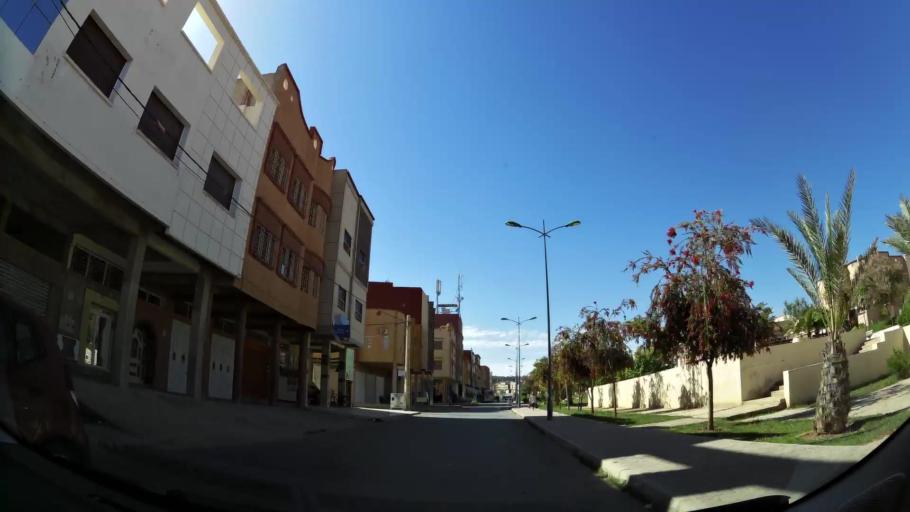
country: MA
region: Oriental
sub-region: Oujda-Angad
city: Oujda
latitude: 34.6577
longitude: -1.8849
